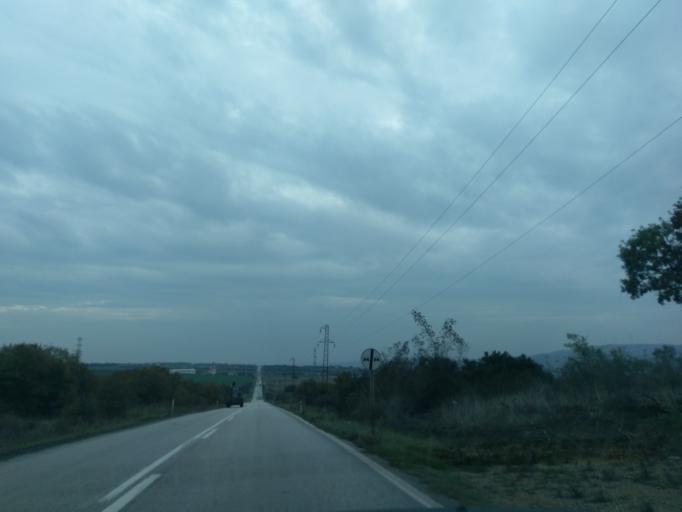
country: TR
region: Istanbul
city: Canta
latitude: 41.1540
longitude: 28.1068
